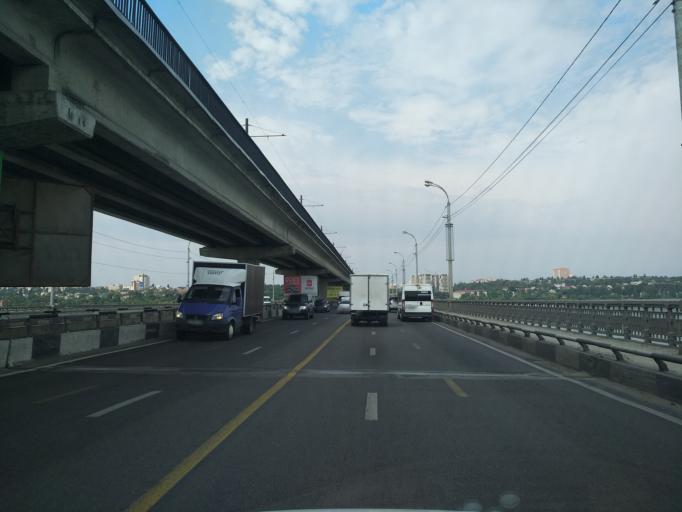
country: RU
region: Voronezj
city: Voronezh
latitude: 51.6896
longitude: 39.2486
